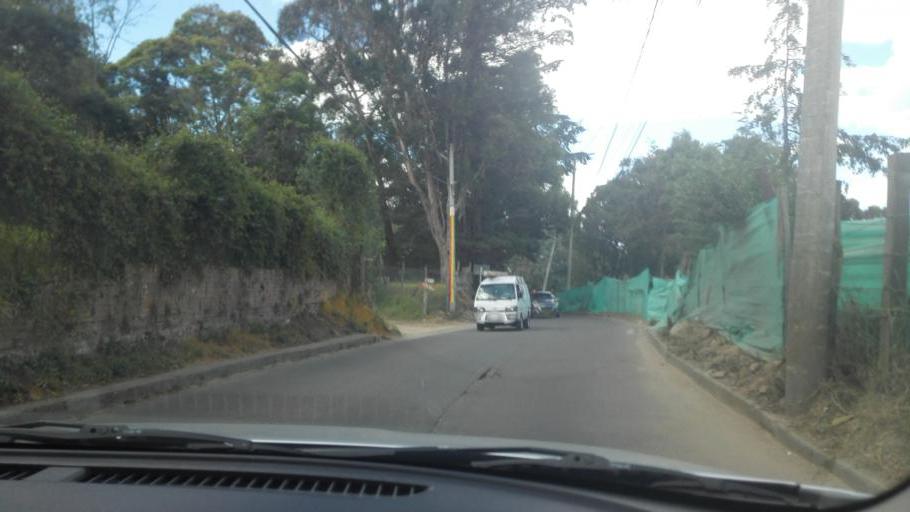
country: CO
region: Cundinamarca
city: Cota
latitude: 4.7398
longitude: -74.0734
